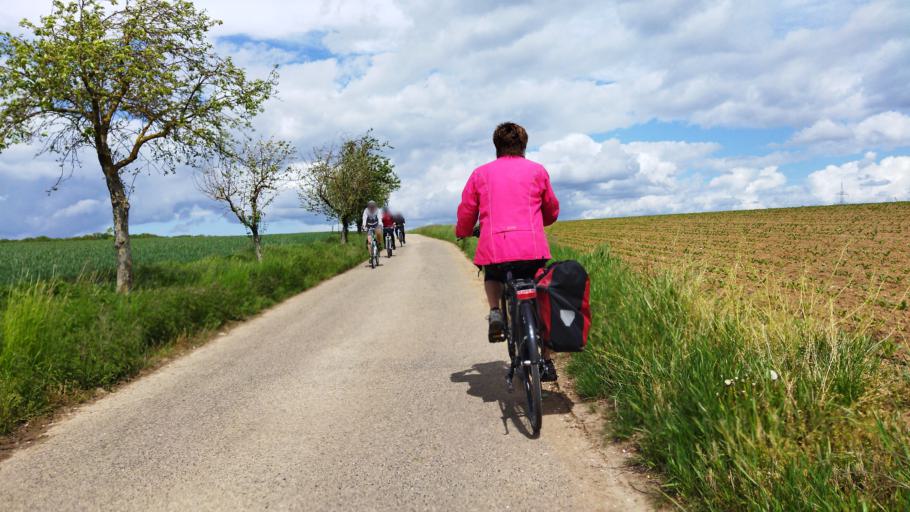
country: DE
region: Baden-Wuerttemberg
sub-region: Regierungsbezirk Stuttgart
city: Leingarten
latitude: 49.1911
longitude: 9.1208
